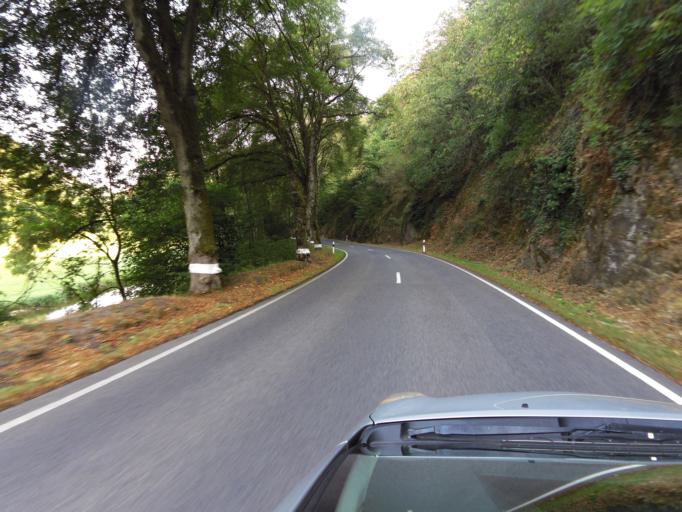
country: LU
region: Diekirch
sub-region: Canton de Diekirch
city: Bourscheid
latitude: 49.9274
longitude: 6.0769
